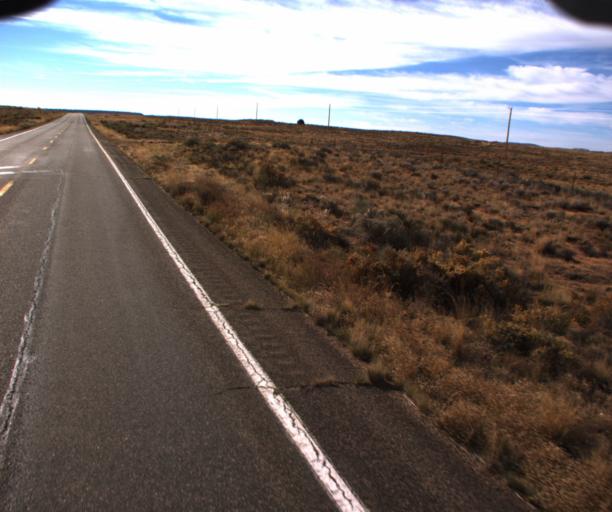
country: US
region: Arizona
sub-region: Coconino County
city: LeChee
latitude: 36.7196
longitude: -111.2763
